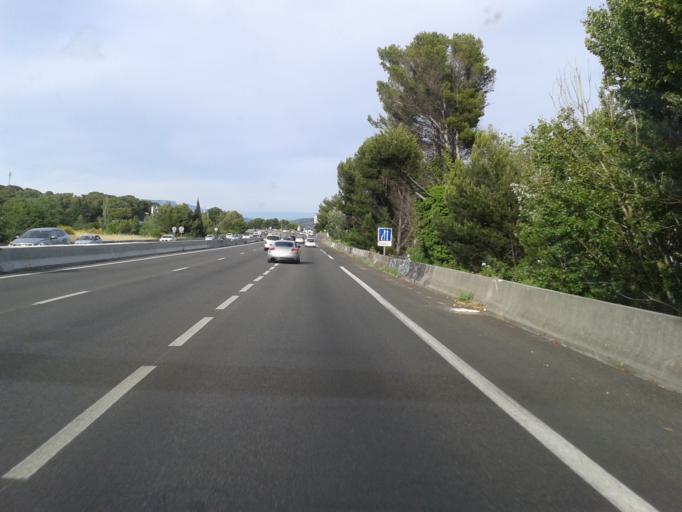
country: FR
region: Provence-Alpes-Cote d'Azur
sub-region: Departement des Bouches-du-Rhone
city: Cabries
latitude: 43.4269
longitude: 5.3829
